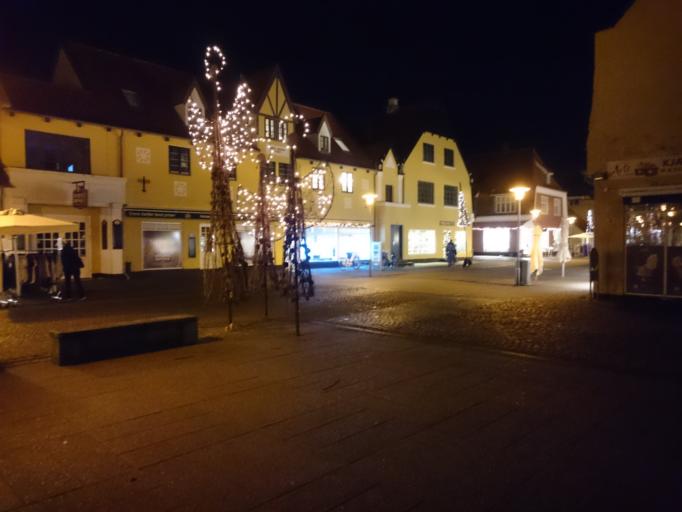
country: DK
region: North Denmark
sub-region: Frederikshavn Kommune
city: Skagen
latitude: 57.7220
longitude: 10.5876
